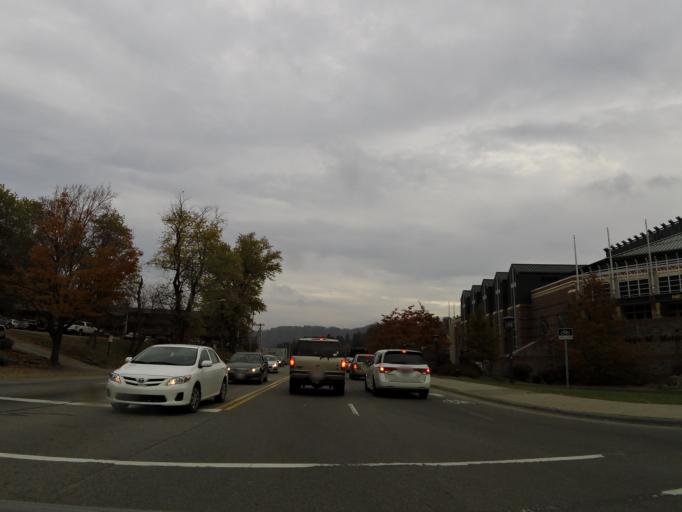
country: US
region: North Carolina
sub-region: Watauga County
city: Boone
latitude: 36.2117
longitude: -81.6755
